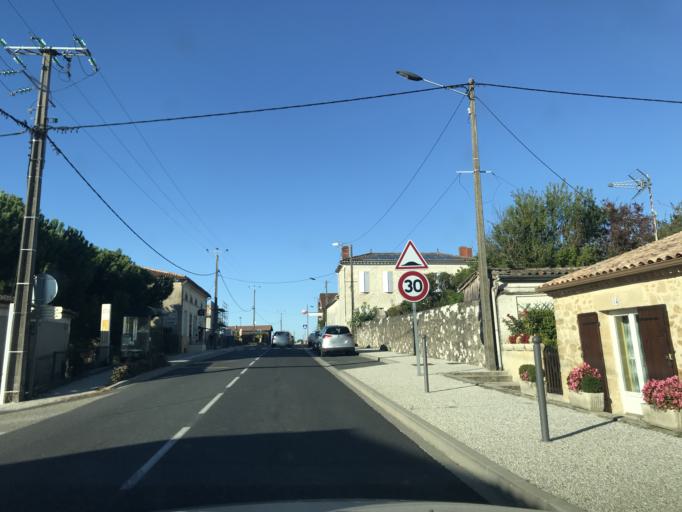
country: FR
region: Aquitaine
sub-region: Departement de la Gironde
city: Saint-Macaire
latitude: 44.5855
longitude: -0.2126
